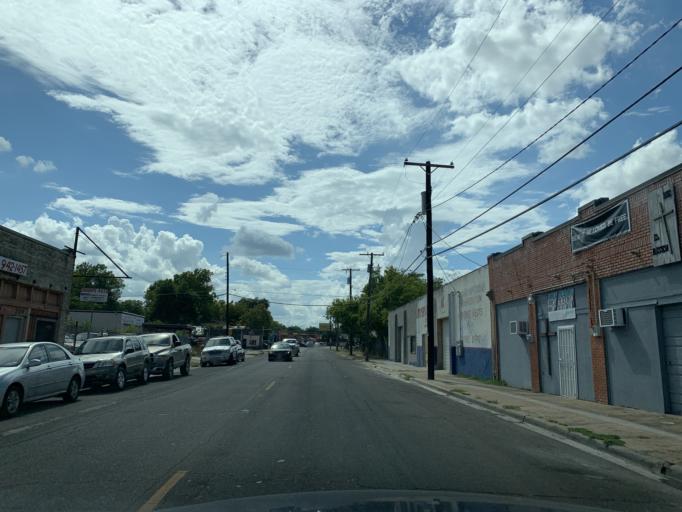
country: US
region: Texas
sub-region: Dallas County
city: Cockrell Hill
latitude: 32.7349
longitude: -96.8531
